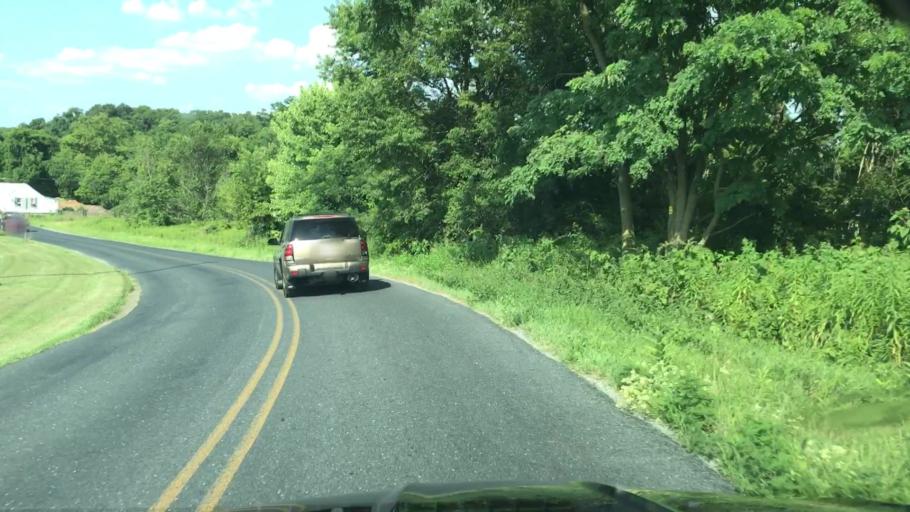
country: US
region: Pennsylvania
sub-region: Cumberland County
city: Boiling Springs
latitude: 40.1827
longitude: -77.1135
